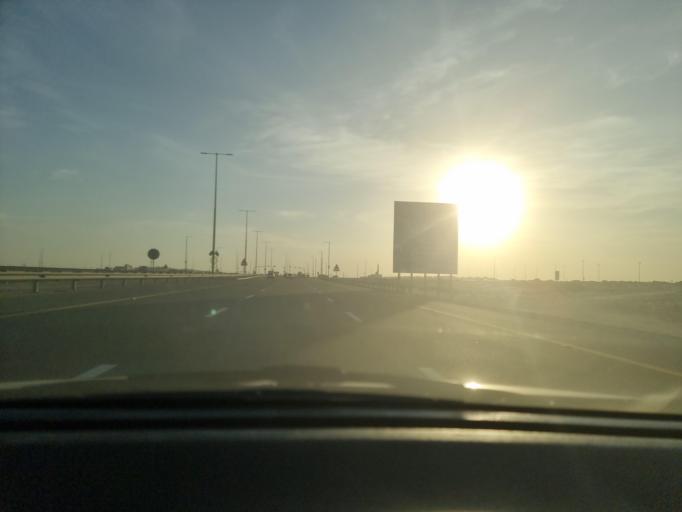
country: AE
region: Abu Dhabi
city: Abu Dhabi
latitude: 24.3403
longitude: 54.7014
